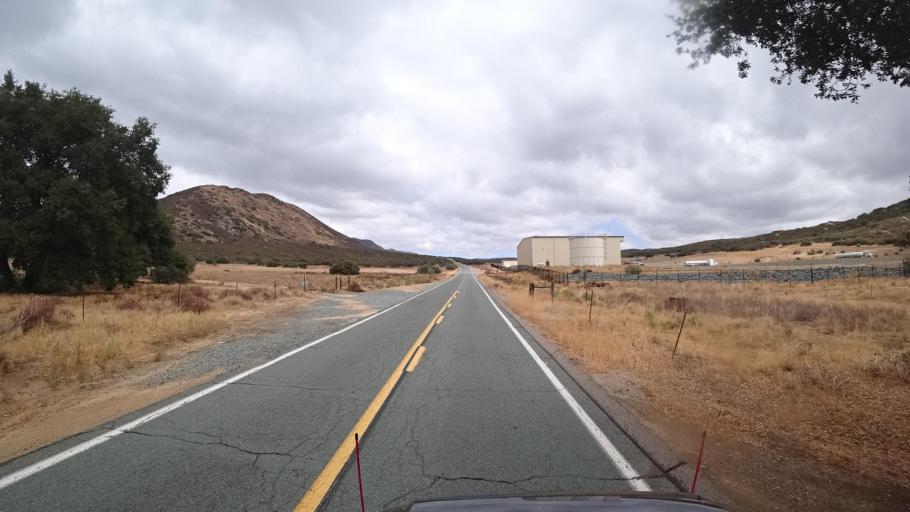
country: US
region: California
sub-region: San Diego County
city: Pine Valley
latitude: 32.7270
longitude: -116.4620
